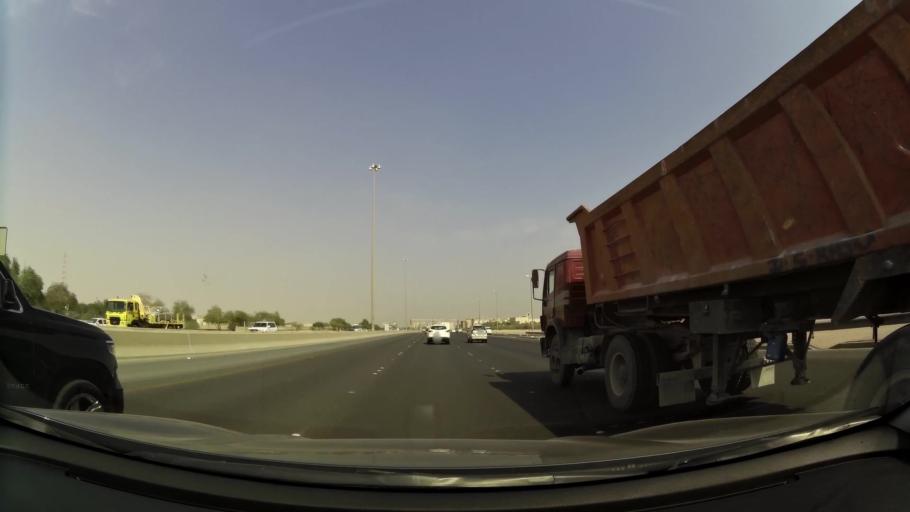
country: KW
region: Al Ahmadi
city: Al Fahahil
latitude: 29.0805
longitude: 48.1138
